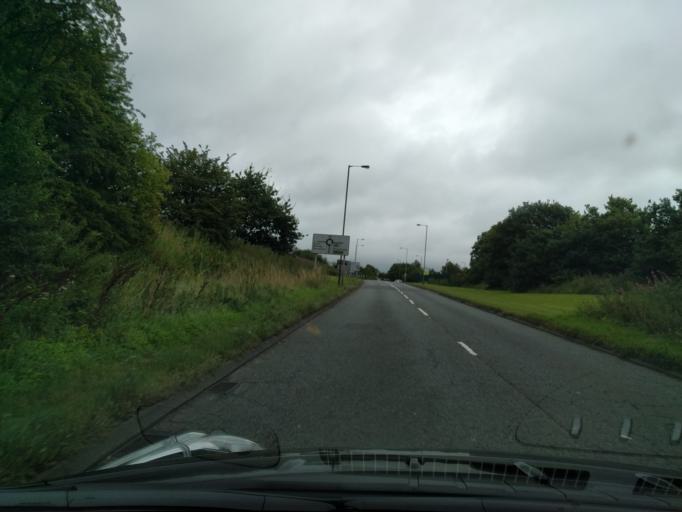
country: GB
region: England
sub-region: Borough of Wigan
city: Ashton in Makerfield
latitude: 53.4737
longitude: -2.6584
